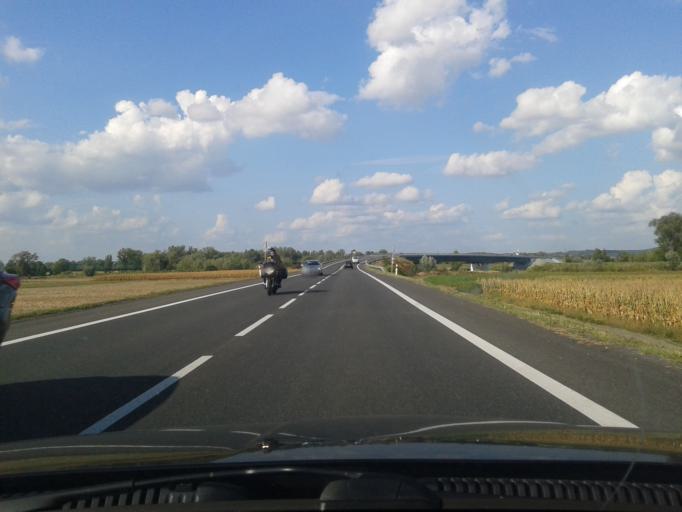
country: PL
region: Silesian Voivodeship
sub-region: Powiat wodzislawski
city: Olza
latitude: 49.9493
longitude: 18.3276
